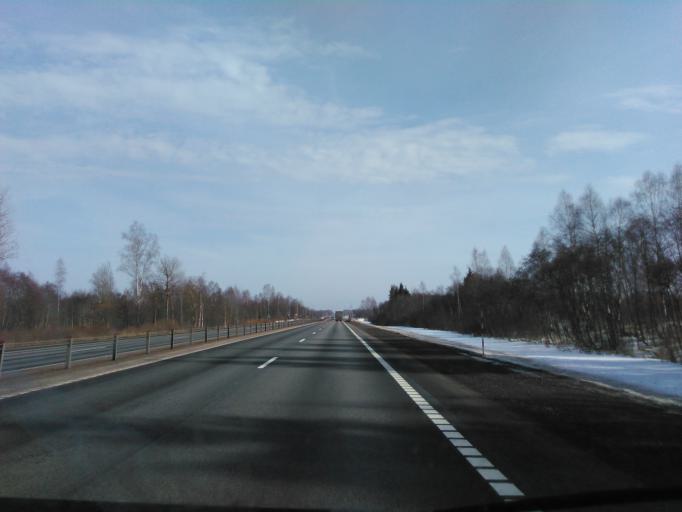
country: BY
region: Vitebsk
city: Dubrowna
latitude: 54.6898
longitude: 30.9247
